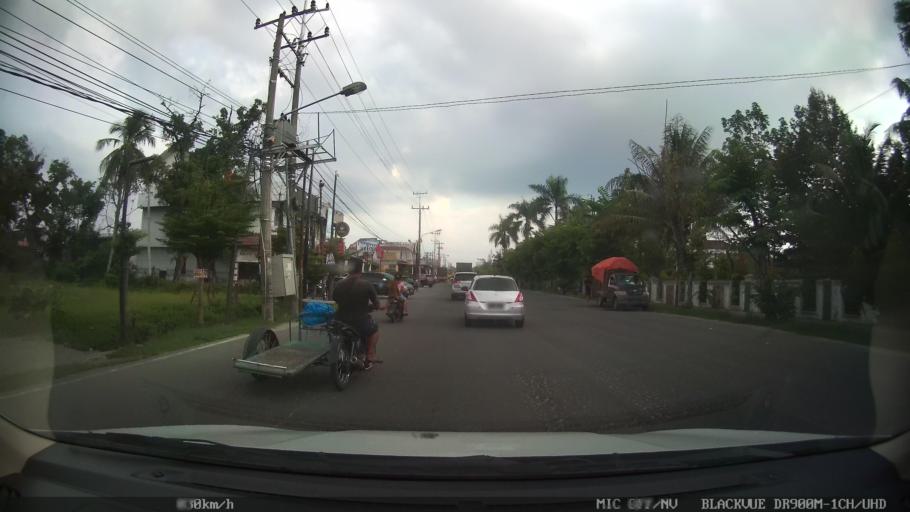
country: ID
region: North Sumatra
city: Sunggal
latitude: 3.5283
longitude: 98.6199
